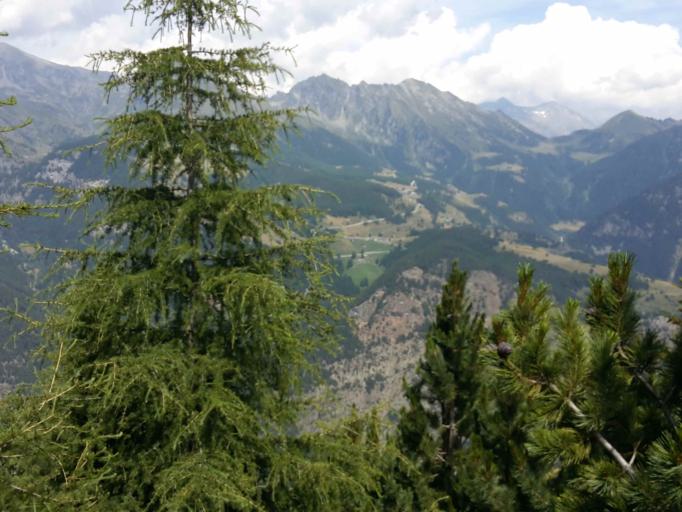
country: IT
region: Aosta Valley
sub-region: Valle d'Aosta
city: Brusson
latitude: 45.7484
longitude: 7.7192
